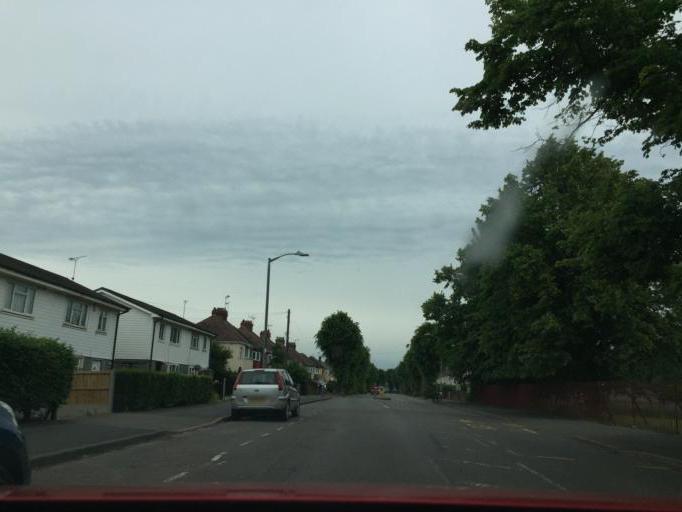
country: GB
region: England
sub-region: Warwickshire
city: Nuneaton
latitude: 52.5167
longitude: -1.4783
